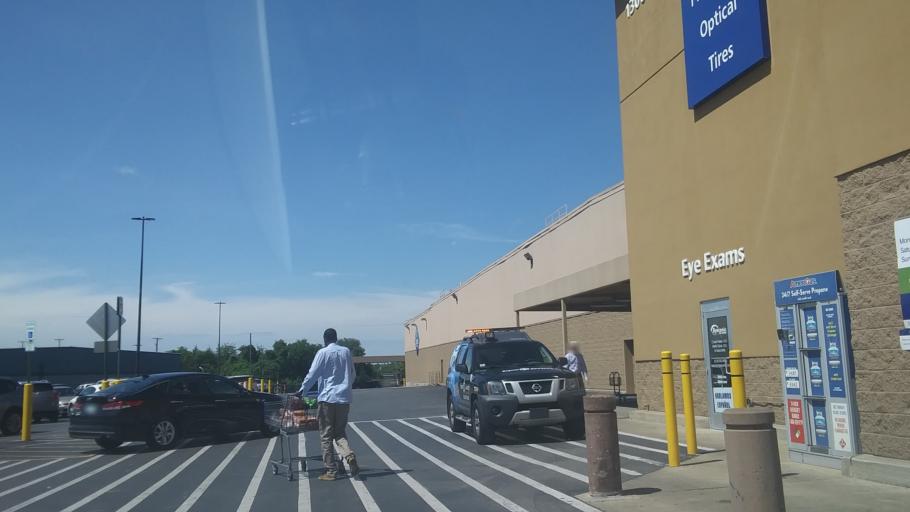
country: US
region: Tennessee
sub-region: Davidson County
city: Oak Hill
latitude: 36.0867
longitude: -86.6905
